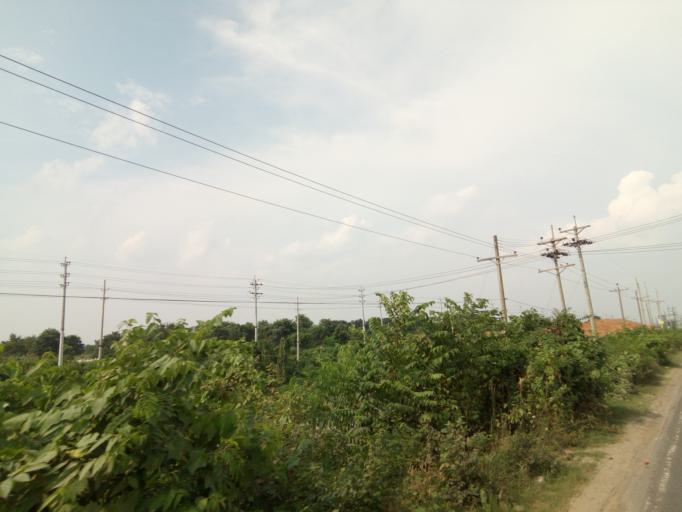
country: BD
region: Dhaka
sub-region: Dhaka
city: Dhaka
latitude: 23.6719
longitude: 90.4016
